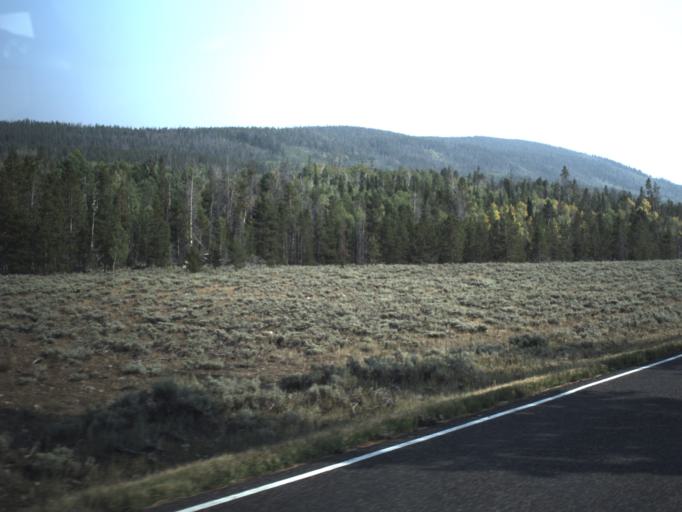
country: US
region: Wyoming
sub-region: Uinta County
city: Evanston
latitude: 40.8818
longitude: -110.8317
